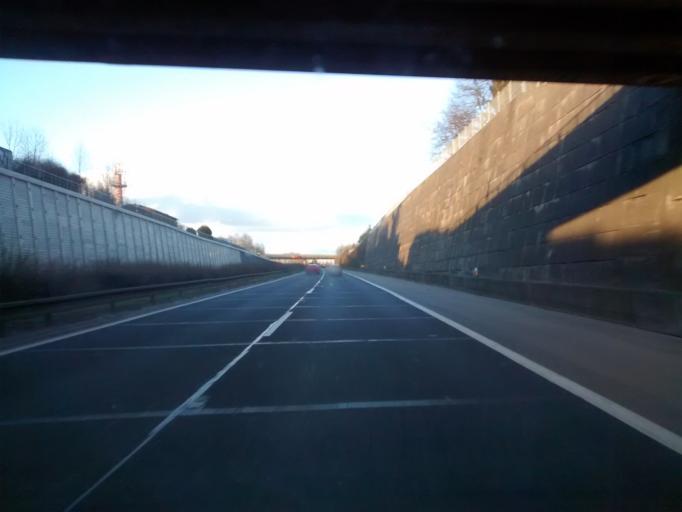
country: CZ
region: Praha
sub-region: Praha 20
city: Horni Pocernice
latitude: 50.1009
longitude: 14.6119
